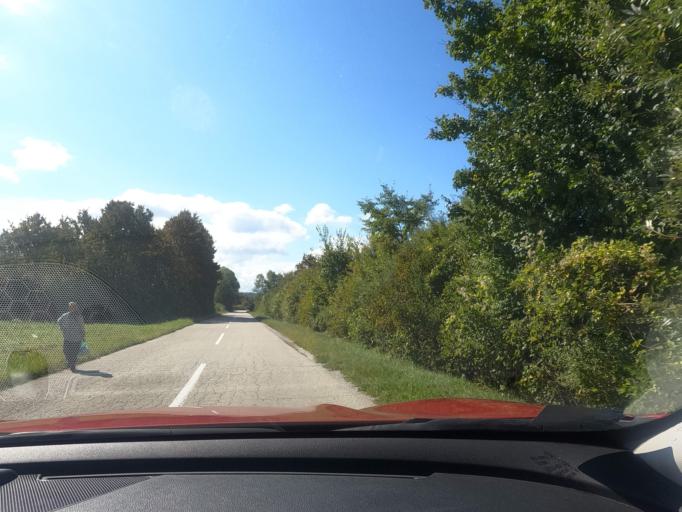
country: BA
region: Federation of Bosnia and Herzegovina
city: Vrnograc
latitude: 45.2553
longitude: 15.9455
